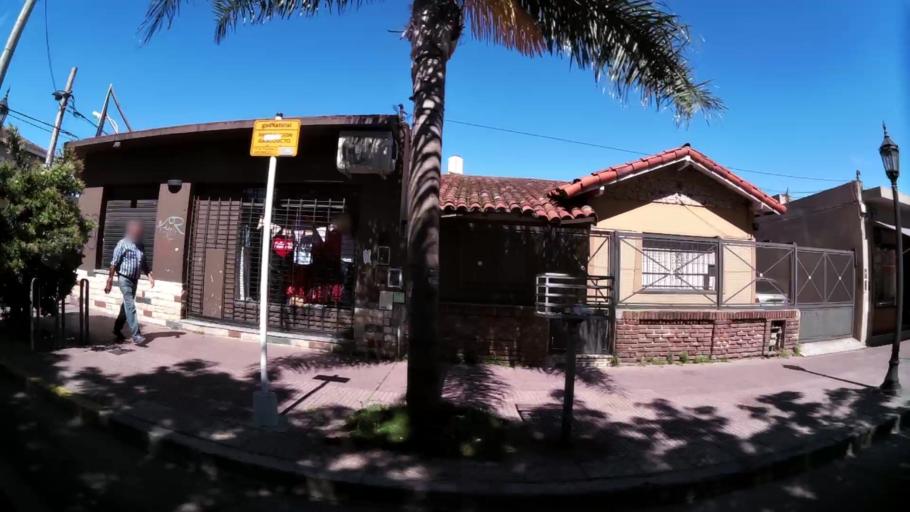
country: AR
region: Buenos Aires
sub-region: Partido de Tigre
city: Tigre
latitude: -34.4870
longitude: -58.6143
